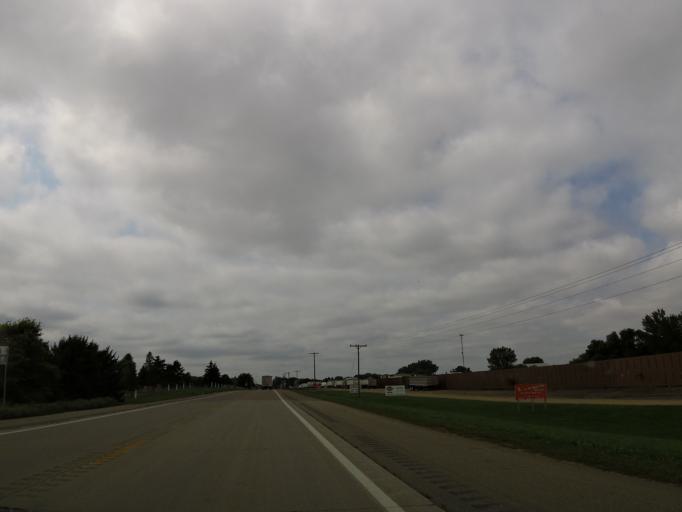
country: US
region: Minnesota
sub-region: Lac qui Parle County
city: Dawson
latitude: 44.9359
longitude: -96.0387
